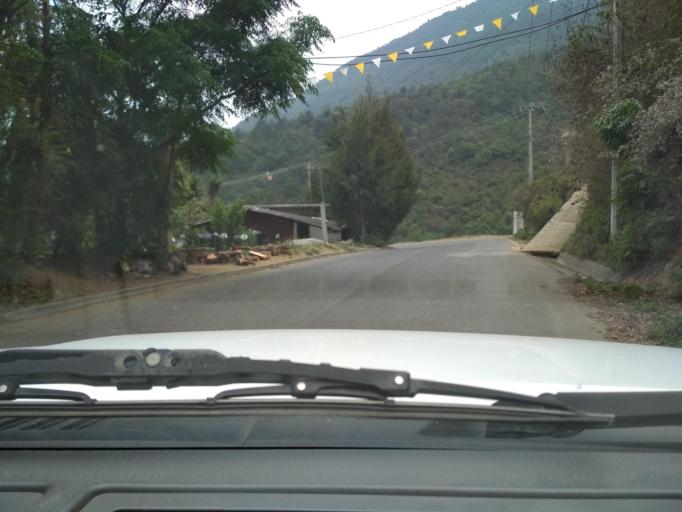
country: MX
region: Veracruz
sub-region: Camerino Z. Mendoza
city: La Cuesta
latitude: 18.7898
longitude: -97.1669
